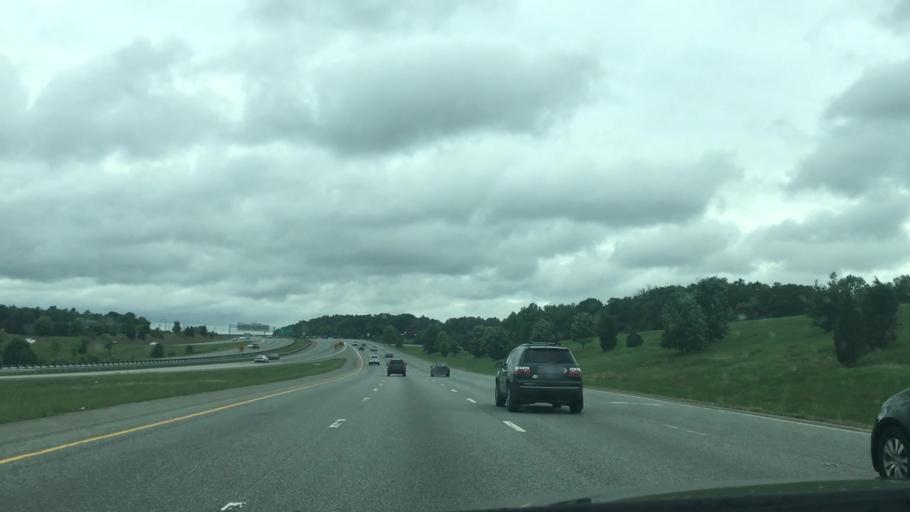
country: US
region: North Carolina
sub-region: Guilford County
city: Jamestown
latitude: 36.0031
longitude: -79.8564
